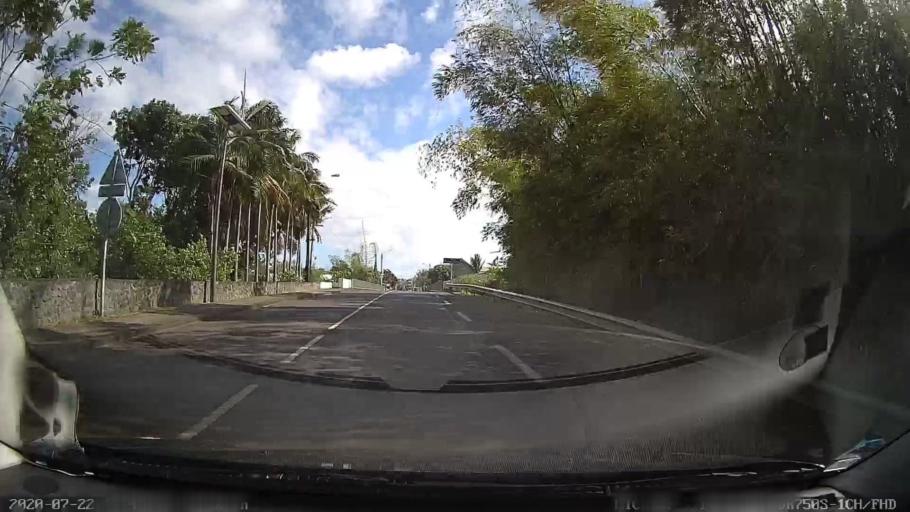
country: RE
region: Reunion
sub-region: Reunion
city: Sainte-Suzanne
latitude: -20.9083
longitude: 55.6093
